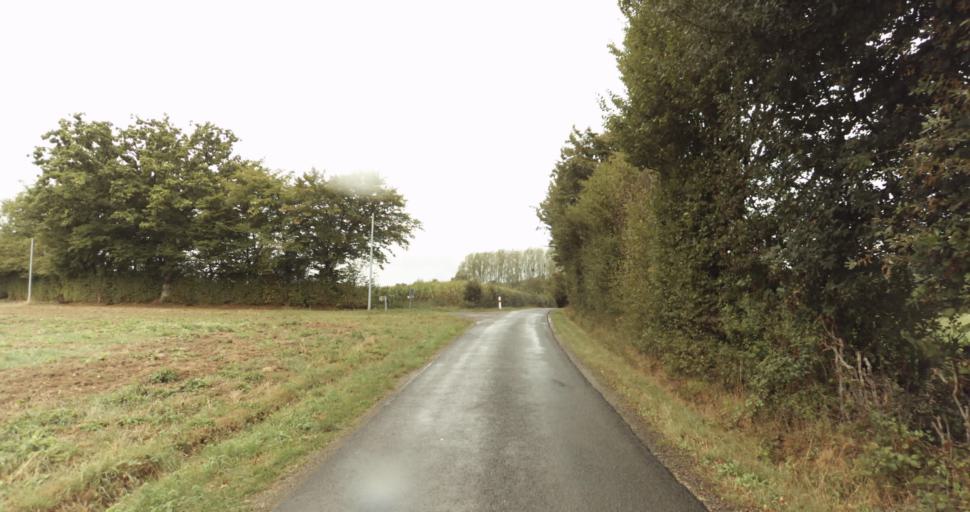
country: FR
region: Lower Normandy
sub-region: Departement de l'Orne
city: Sainte-Gauburge-Sainte-Colombe
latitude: 48.6889
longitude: 0.4160
